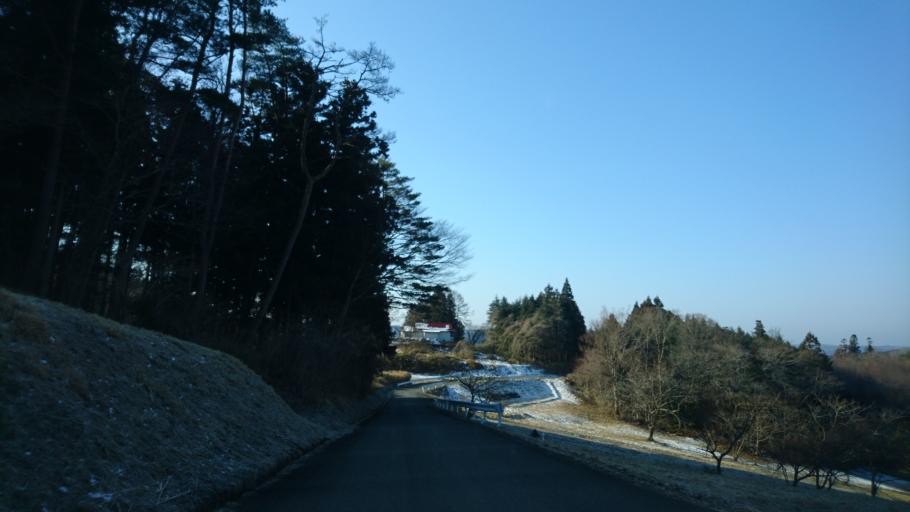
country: JP
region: Iwate
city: Ichinoseki
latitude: 38.9146
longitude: 141.2901
